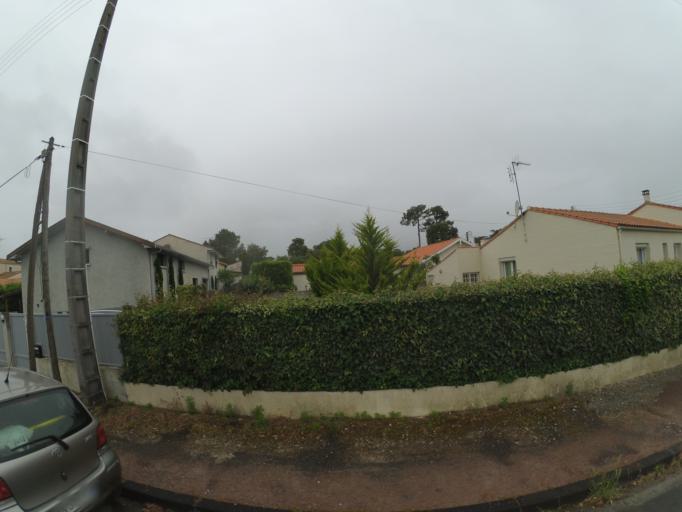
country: FR
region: Poitou-Charentes
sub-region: Departement de la Charente-Maritime
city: Saint-Georges-de-Didonne
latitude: 45.6155
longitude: -1.0018
